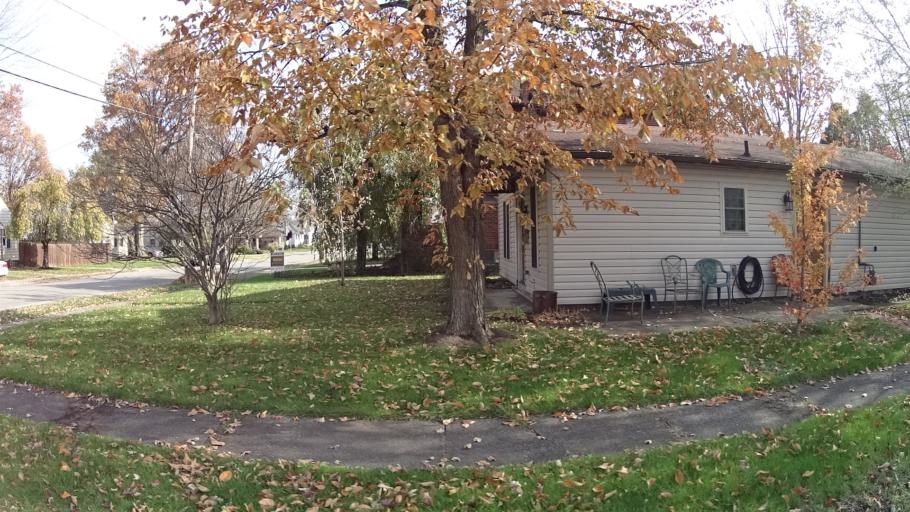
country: US
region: Ohio
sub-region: Lorain County
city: Elyria
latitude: 41.3686
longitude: -82.0838
